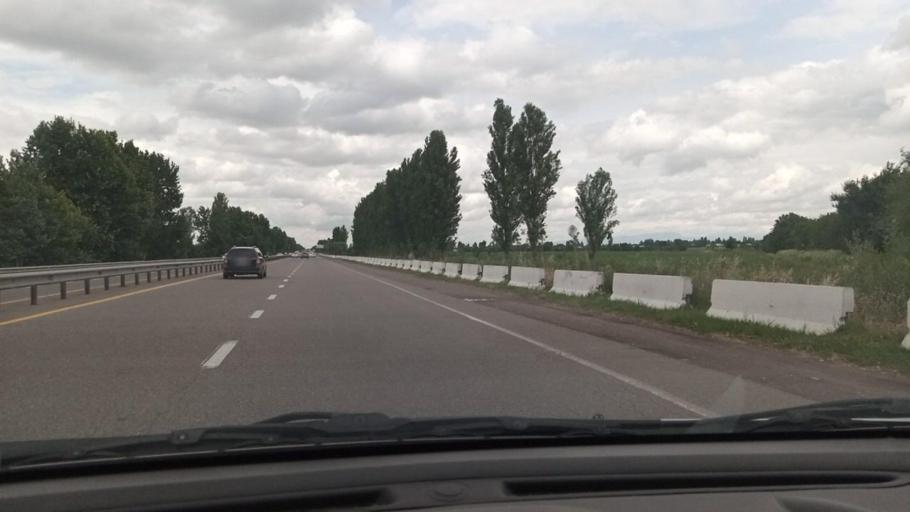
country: UZ
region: Toshkent Shahri
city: Bektemir
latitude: 41.2104
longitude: 69.4028
